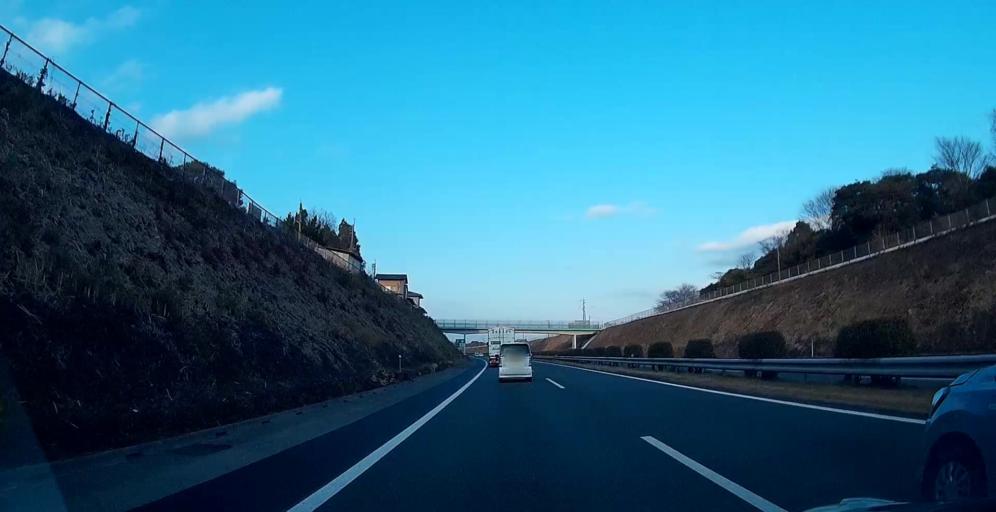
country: JP
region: Kumamoto
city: Uto
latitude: 32.6999
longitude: 130.7502
